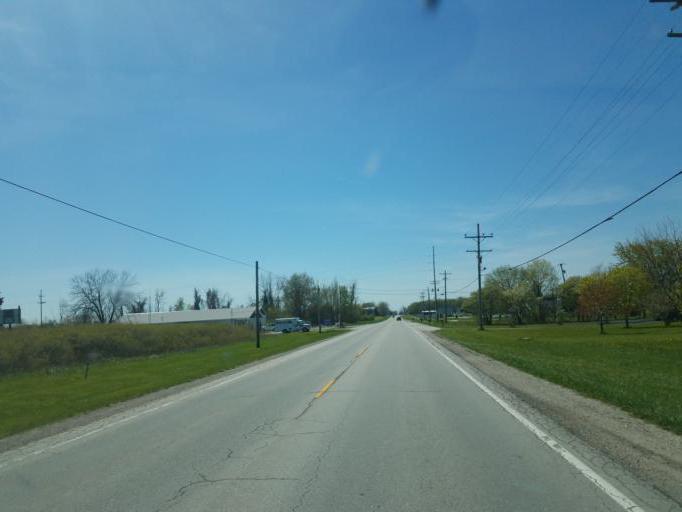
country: US
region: Ohio
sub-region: Ottawa County
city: Port Clinton
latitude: 41.5083
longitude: -82.8612
